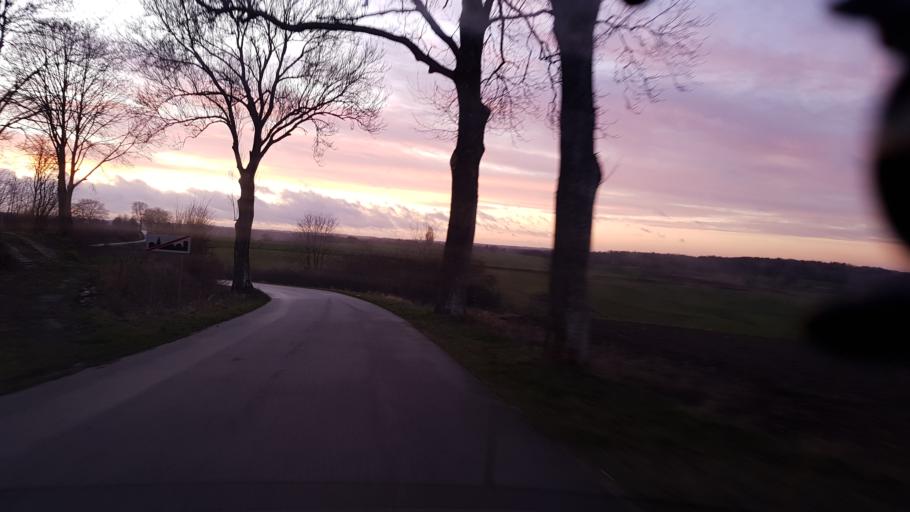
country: PL
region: Pomeranian Voivodeship
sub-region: Powiat bytowski
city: Tuchomie
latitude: 54.1326
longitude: 17.3614
